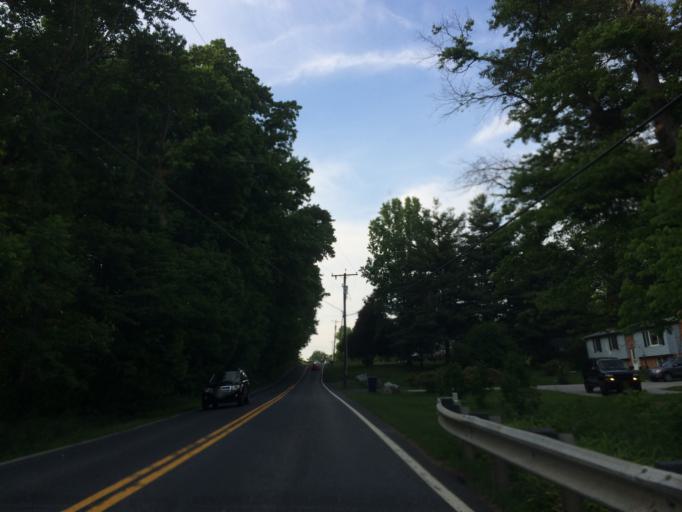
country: US
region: Maryland
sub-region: Carroll County
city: Eldersburg
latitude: 39.4215
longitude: -77.0102
